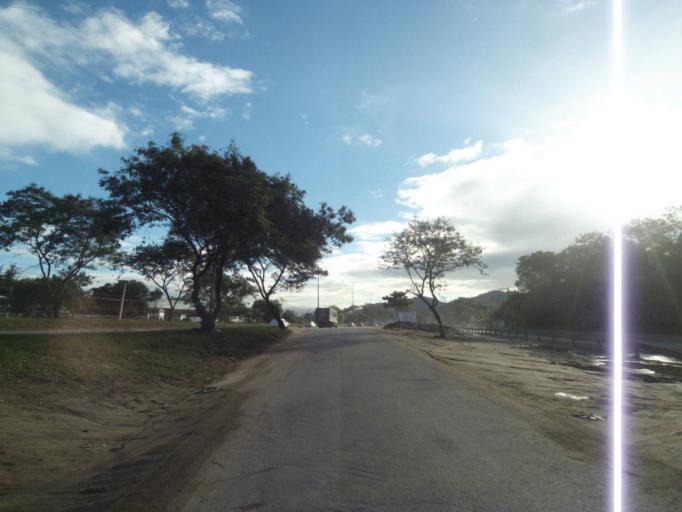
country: BR
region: Rio de Janeiro
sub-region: Nilopolis
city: Nilopolis
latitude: -22.8564
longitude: -43.4753
